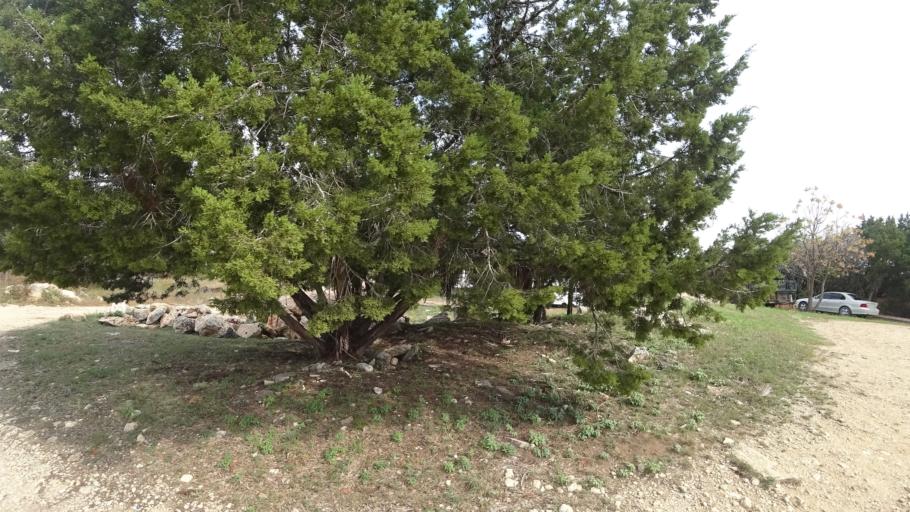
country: US
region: Texas
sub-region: Travis County
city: Hudson Bend
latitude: 30.3891
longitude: -97.9278
